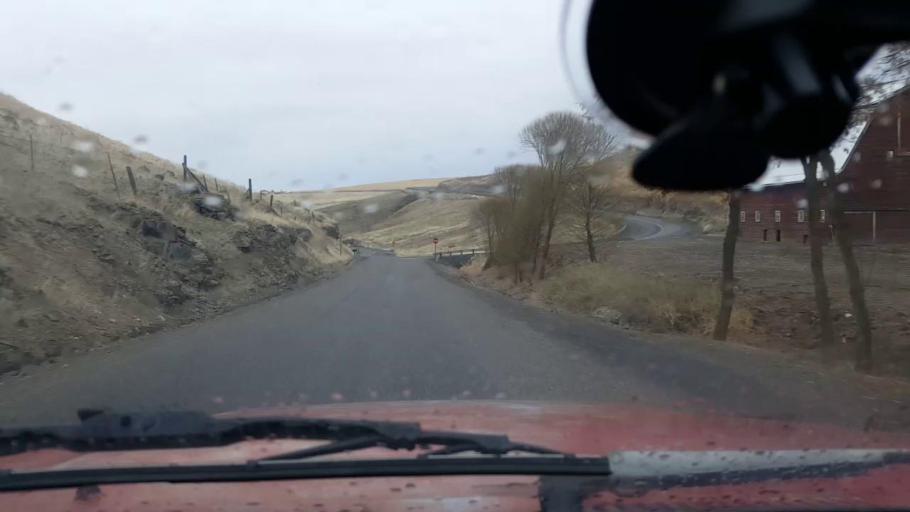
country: US
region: Washington
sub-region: Asotin County
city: Clarkston Heights-Vineland
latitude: 46.3873
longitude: -117.1390
